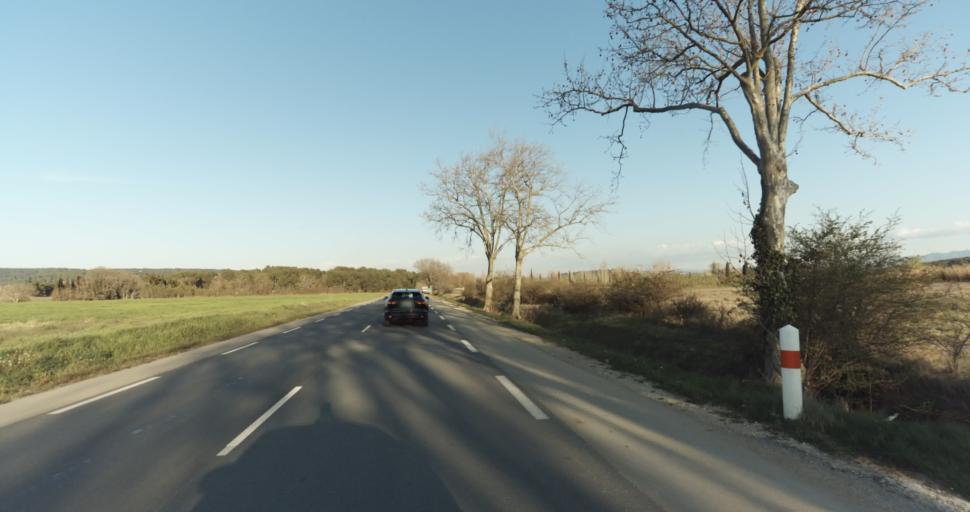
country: FR
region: Provence-Alpes-Cote d'Azur
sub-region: Departement des Bouches-du-Rhone
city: Eguilles
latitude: 43.5458
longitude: 5.3355
